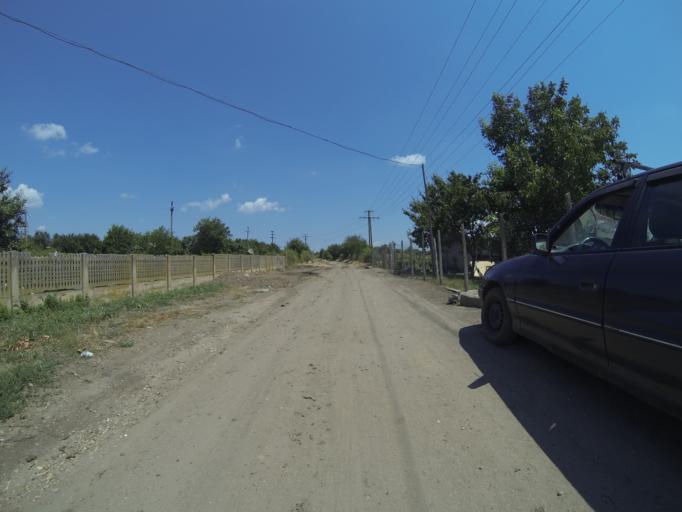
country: RO
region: Dolj
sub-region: Comuna Segarcea
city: Segarcea
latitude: 44.0866
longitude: 23.7523
